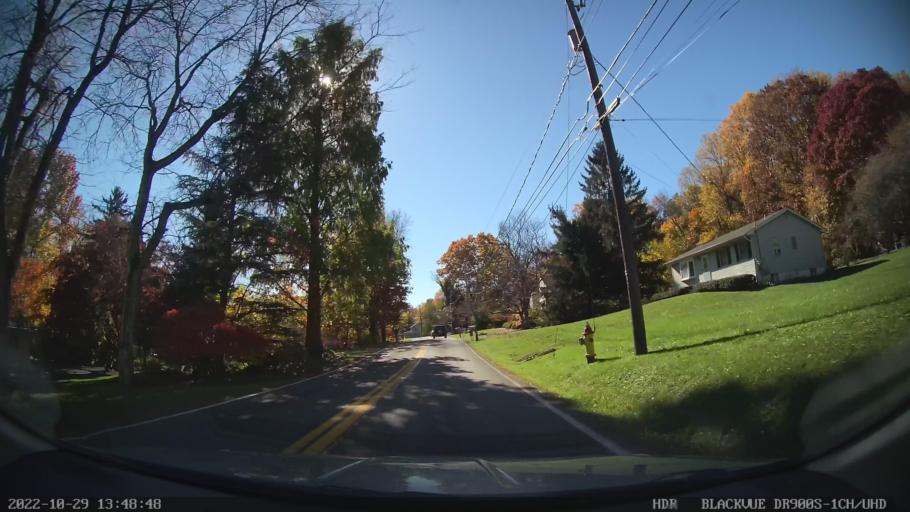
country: US
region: Pennsylvania
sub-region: Lehigh County
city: Emmaus
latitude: 40.5459
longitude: -75.4533
